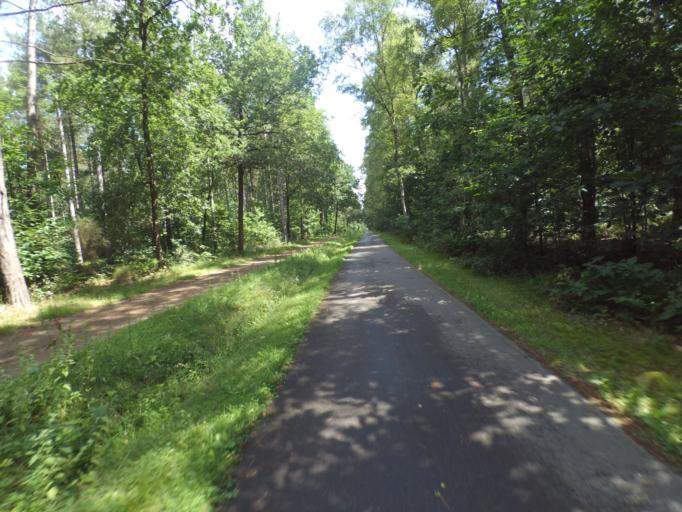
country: BE
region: Flanders
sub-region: Provincie Limburg
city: Opglabbeek
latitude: 51.0804
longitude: 5.6266
